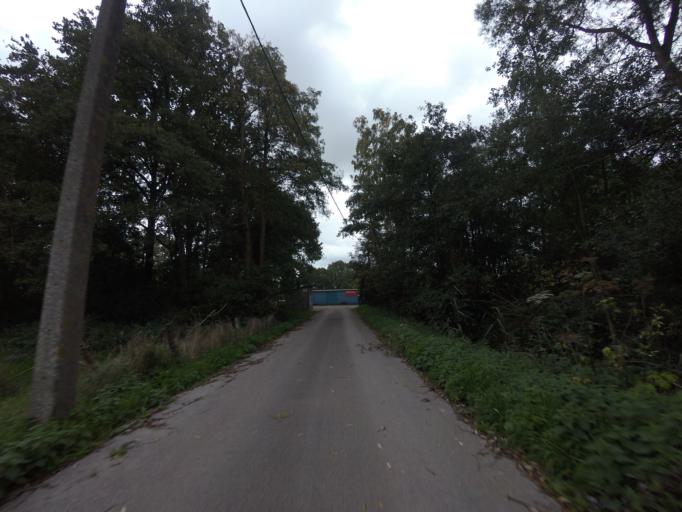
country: BE
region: Flanders
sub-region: Provincie Antwerpen
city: Rumst
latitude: 51.0665
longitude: 4.4122
